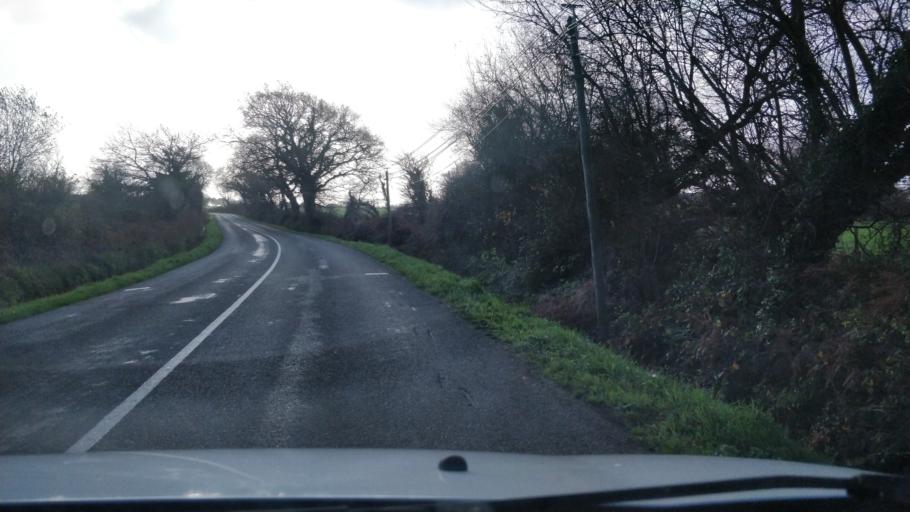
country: FR
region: Pays de la Loire
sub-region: Departement de la Loire-Atlantique
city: Guerande
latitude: 47.3479
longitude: -2.4311
